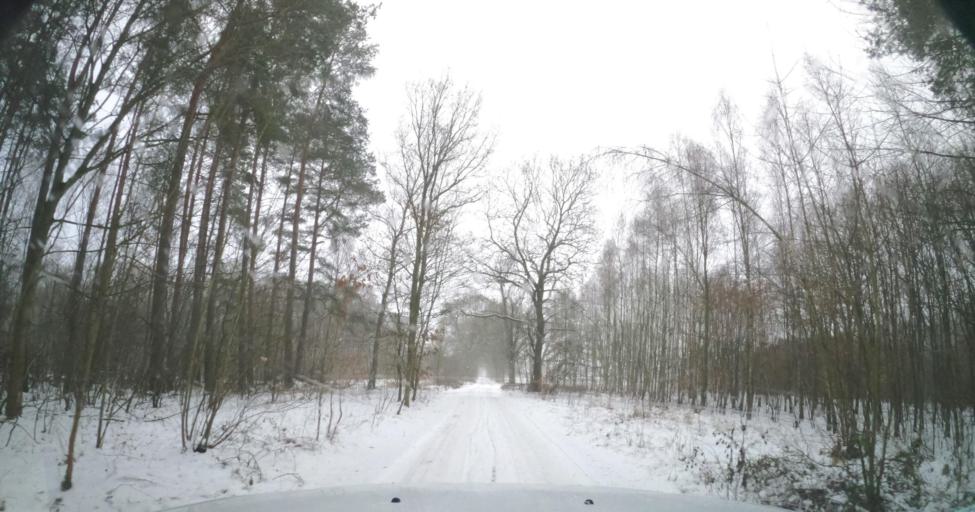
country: PL
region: West Pomeranian Voivodeship
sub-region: Powiat kamienski
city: Golczewo
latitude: 53.7709
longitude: 14.9434
